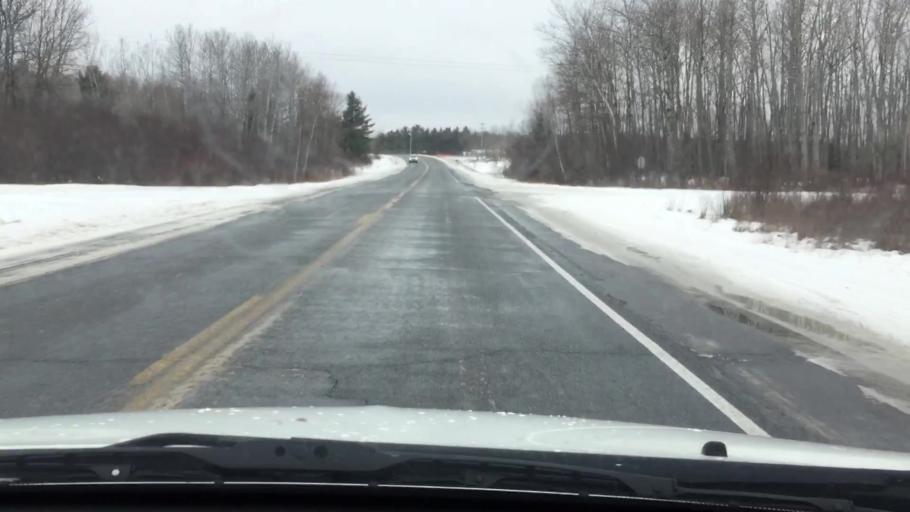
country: US
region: Michigan
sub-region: Wexford County
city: Cadillac
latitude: 44.1172
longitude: -85.4425
